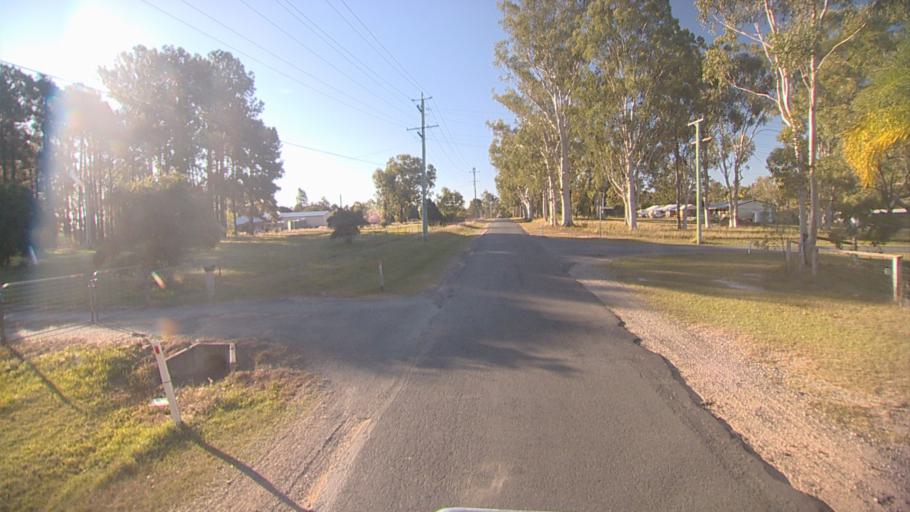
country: AU
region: Queensland
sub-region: Logan
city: Chambers Flat
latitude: -27.7794
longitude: 153.0876
